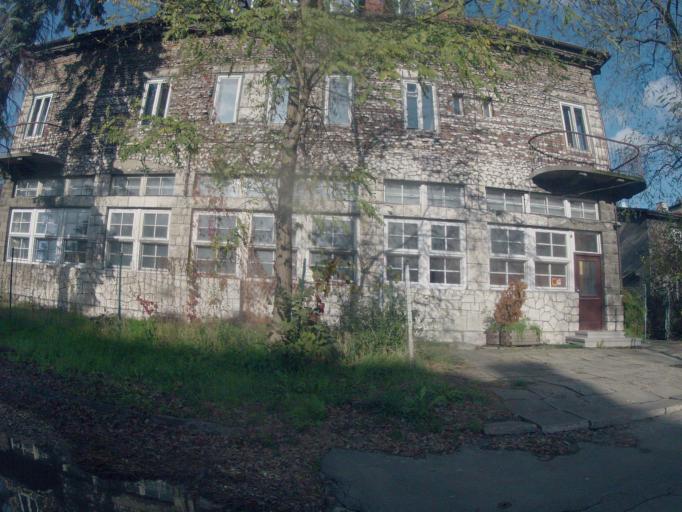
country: PL
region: Lesser Poland Voivodeship
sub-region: Powiat krakowski
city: Rzaska
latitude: 50.0648
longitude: 19.8801
